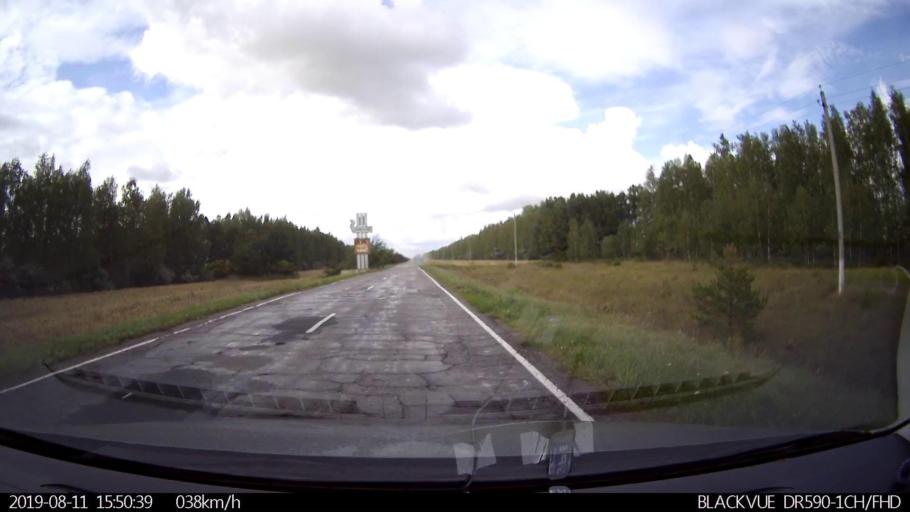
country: RU
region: Ulyanovsk
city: Ignatovka
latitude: 53.9133
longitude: 47.6559
